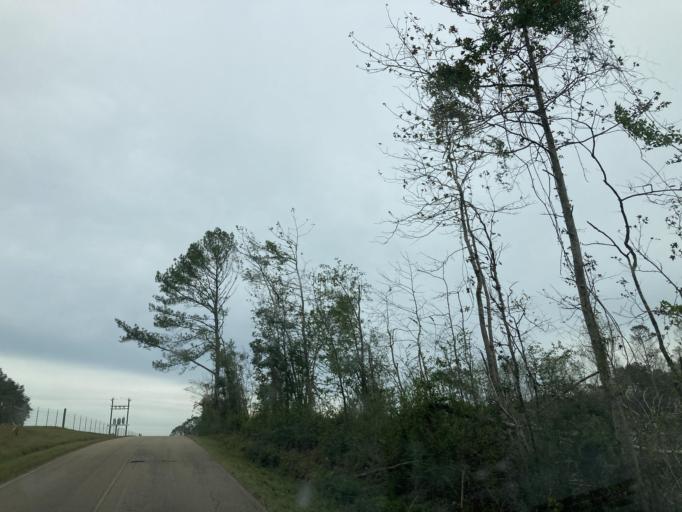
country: US
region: Mississippi
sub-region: Lamar County
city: Lumberton
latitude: 31.0417
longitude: -89.4531
